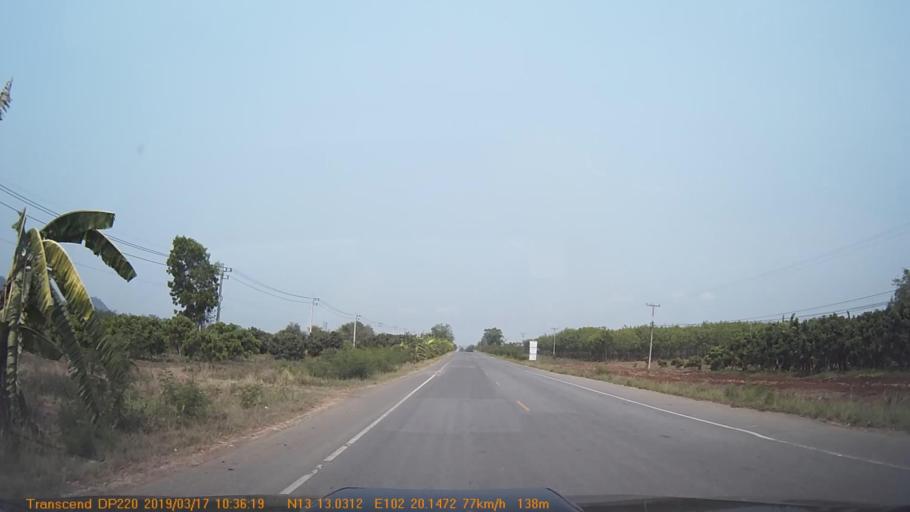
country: TH
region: Chanthaburi
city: Soi Dao
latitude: 13.2173
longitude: 102.3354
